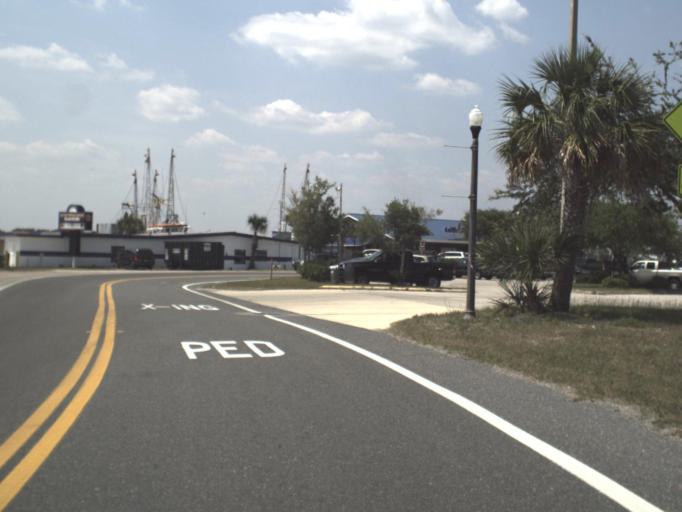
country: US
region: Florida
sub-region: Duval County
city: Atlantic Beach
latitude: 30.3895
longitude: -81.4323
